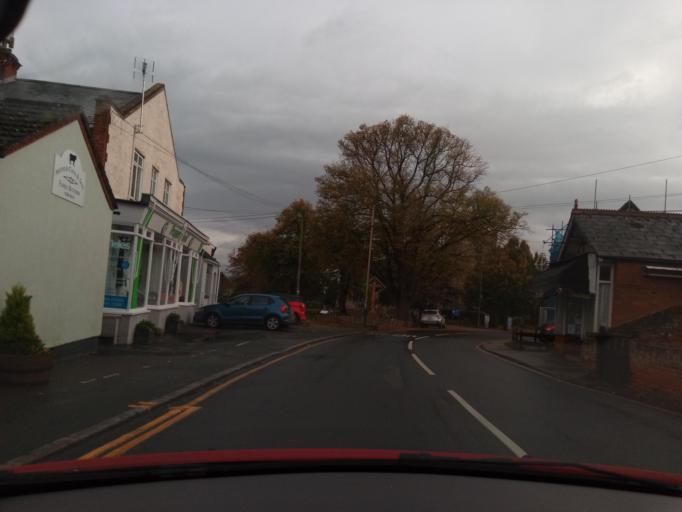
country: GB
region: England
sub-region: Essex
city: West Mersea
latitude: 51.7761
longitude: 0.9113
